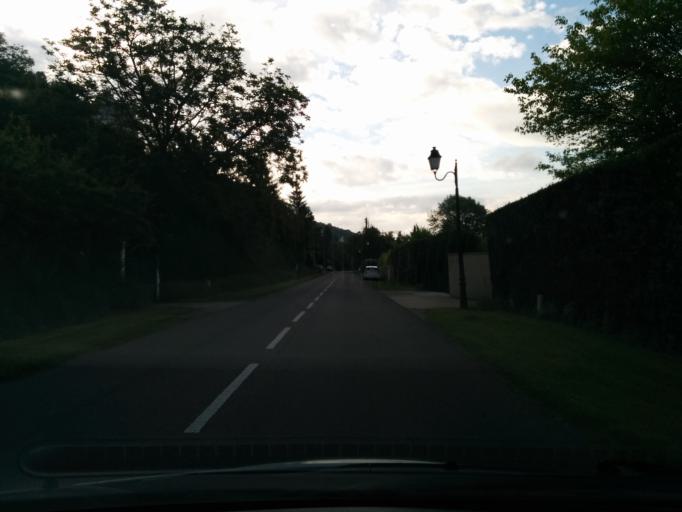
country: FR
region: Haute-Normandie
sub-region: Departement de l'Eure
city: Gasny
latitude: 49.0822
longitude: 1.6633
